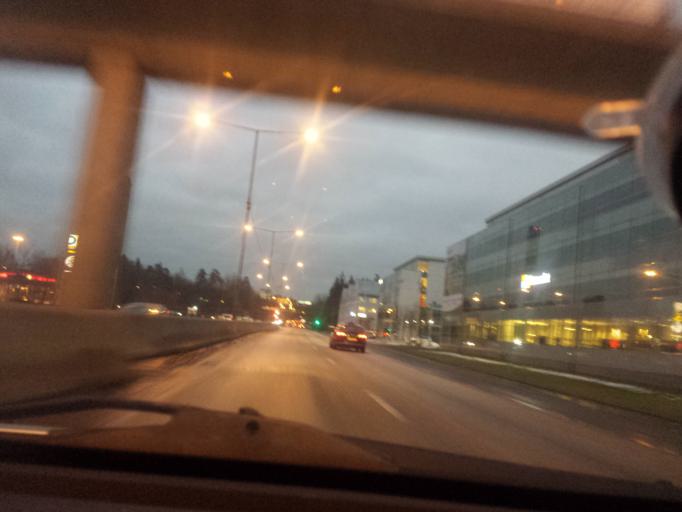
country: SE
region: Stockholm
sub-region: Stockholms Kommun
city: Kista
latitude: 59.4174
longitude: 17.9211
